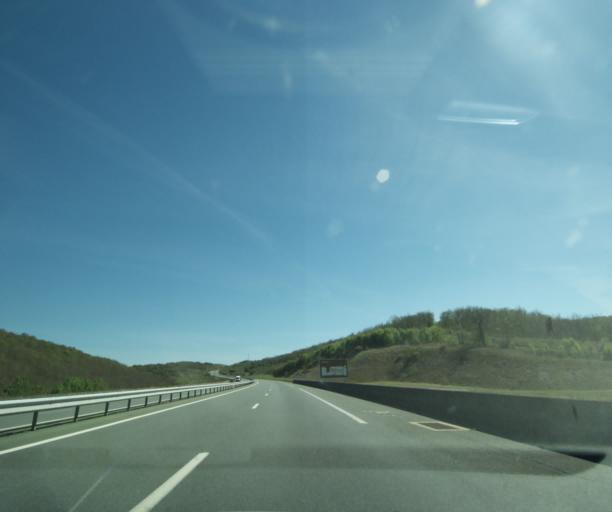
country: FR
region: Midi-Pyrenees
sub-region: Departement du Lot
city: Le Vigan
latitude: 44.7273
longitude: 1.5577
